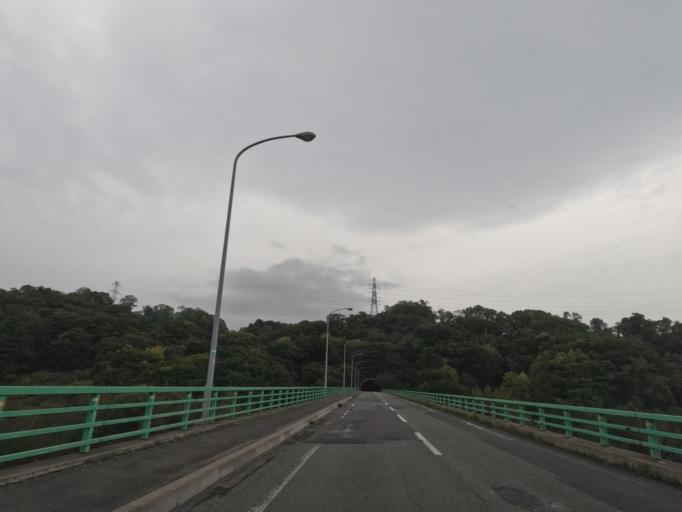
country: JP
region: Hokkaido
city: Date
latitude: 42.5077
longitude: 140.8632
